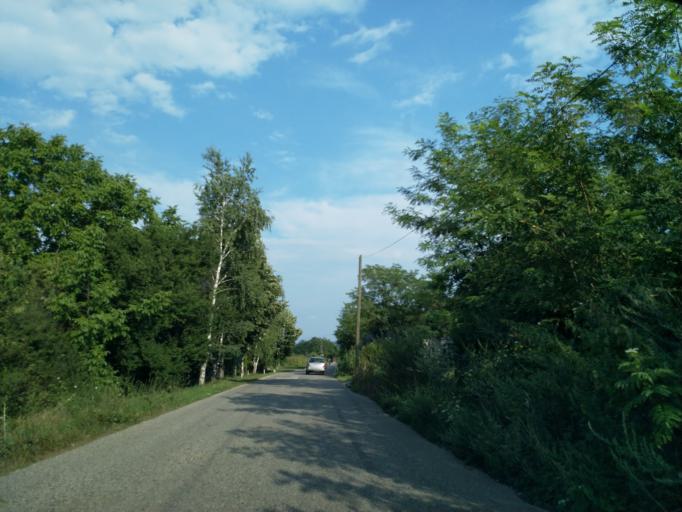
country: RS
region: Central Serbia
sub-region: Pomoravski Okrug
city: Jagodina
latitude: 43.9826
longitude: 21.2228
